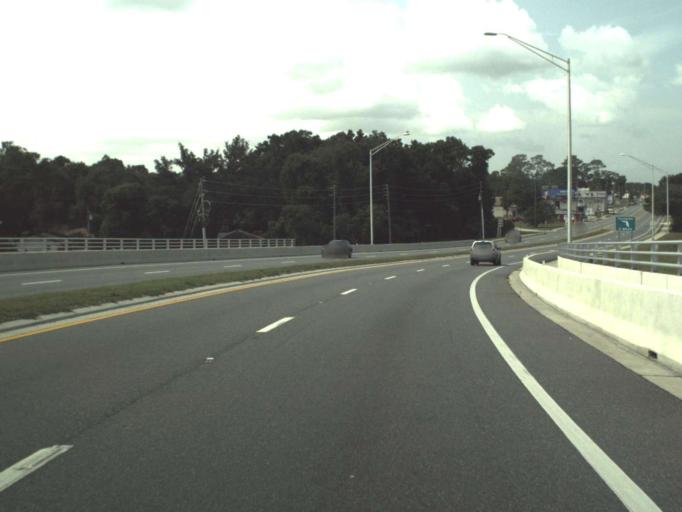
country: US
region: Florida
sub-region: Sumter County
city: Wildwood
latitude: 28.8726
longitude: -82.0365
